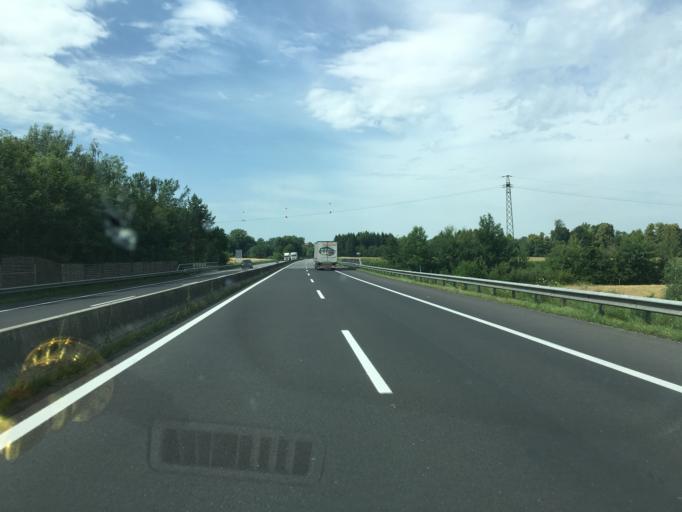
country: AT
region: Upper Austria
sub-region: Politischer Bezirk Kirchdorf an der Krems
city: Micheldorf in Oberoesterreich
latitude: 47.9637
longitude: 14.0969
